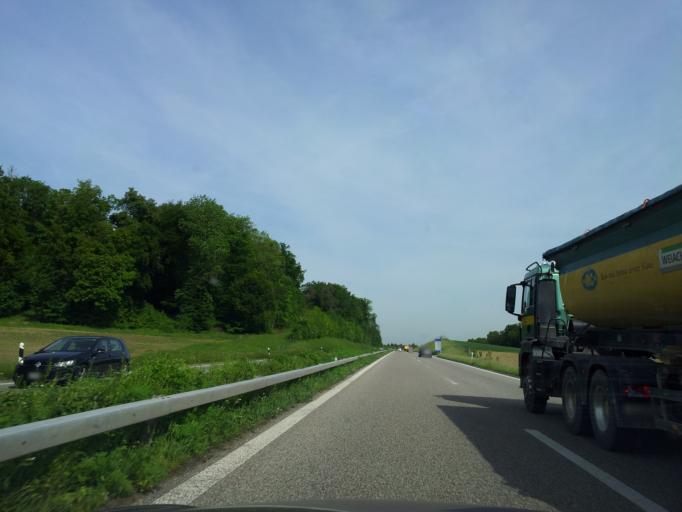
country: CH
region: Zurich
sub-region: Bezirk Buelach
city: Bachenbulach
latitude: 47.4895
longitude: 8.5426
